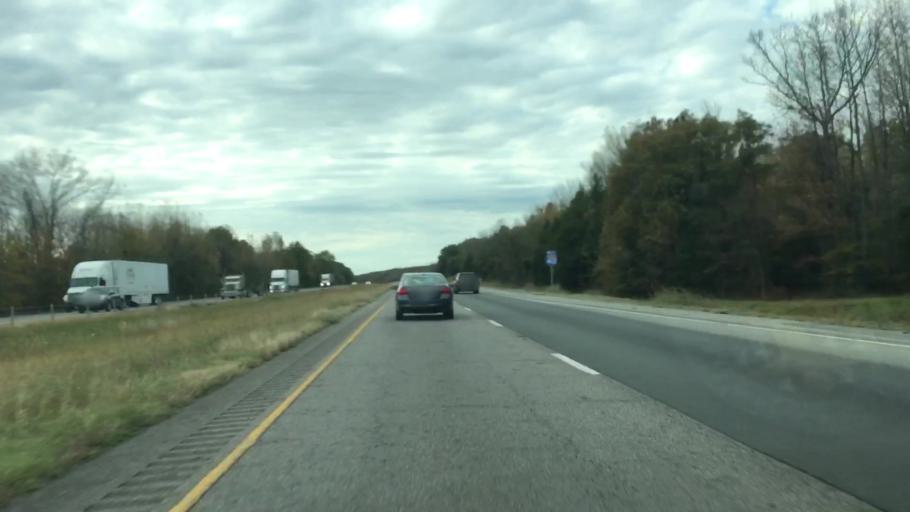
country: US
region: Arkansas
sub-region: Faulkner County
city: Conway
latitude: 35.1551
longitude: -92.5596
